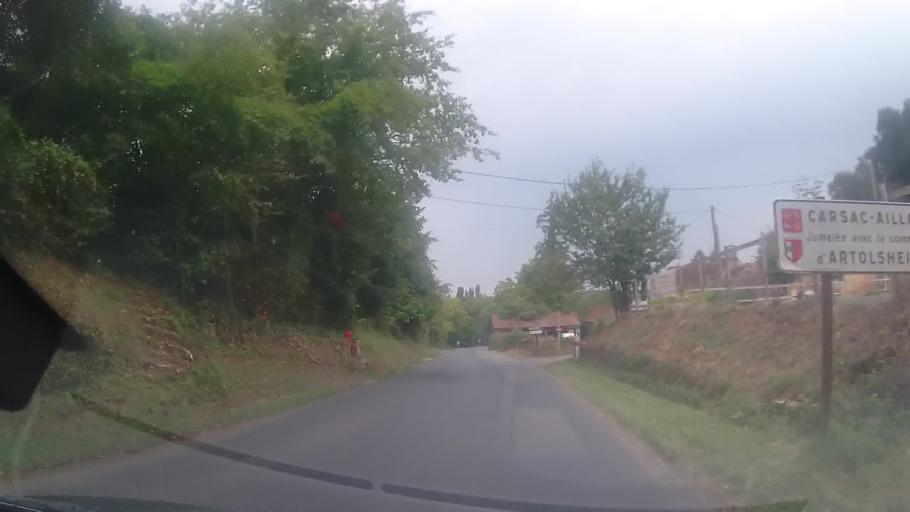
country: FR
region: Aquitaine
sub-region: Departement de la Dordogne
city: Carsac-Aillac
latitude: 44.8382
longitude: 1.2798
